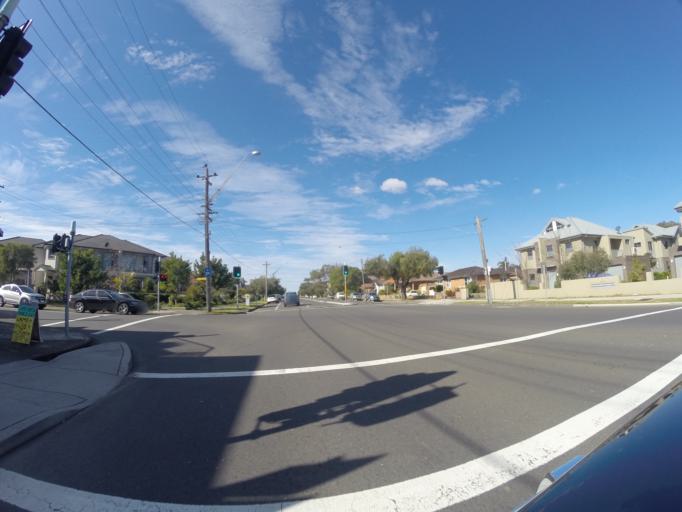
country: AU
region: New South Wales
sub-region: Rockdale
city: Brighton-Le-Sands
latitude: -33.9660
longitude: 151.1489
